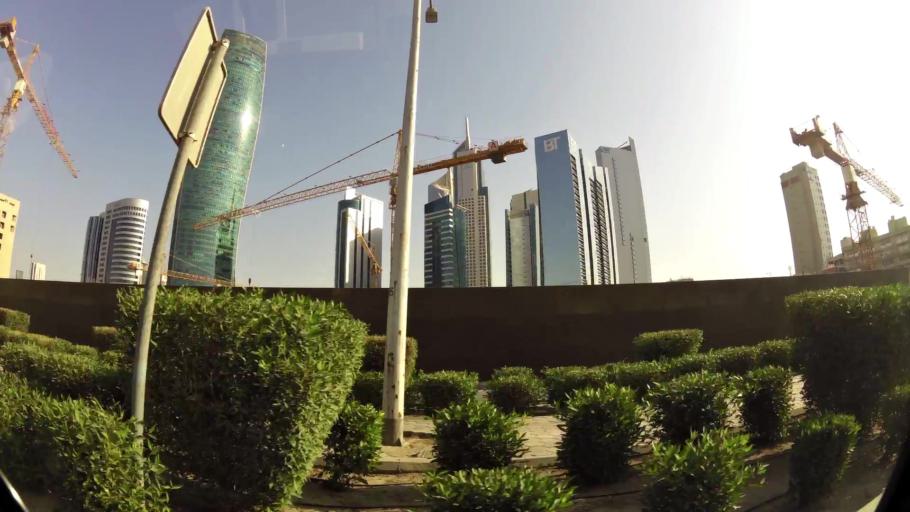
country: KW
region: Al Asimah
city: Kuwait City
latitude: 29.3731
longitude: 47.9863
